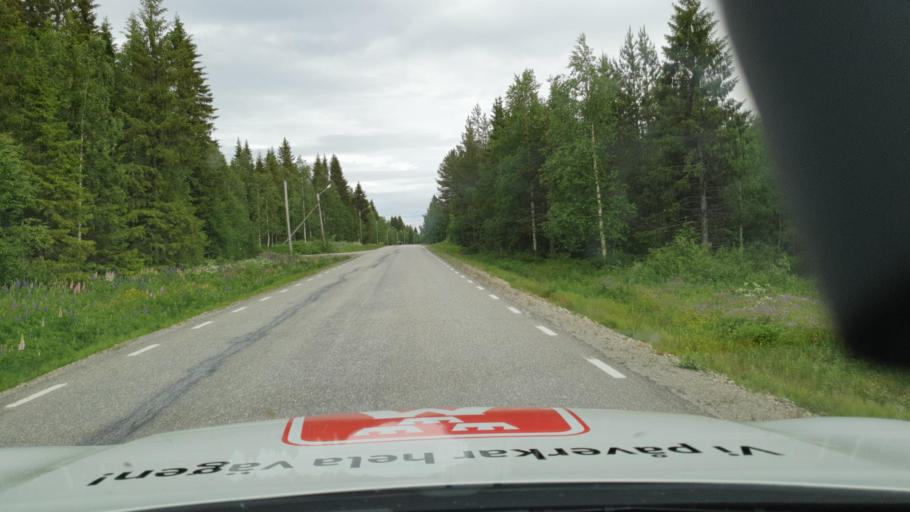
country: SE
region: Vaesterbotten
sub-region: Lycksele Kommun
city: Soderfors
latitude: 64.3635
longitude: 18.0951
